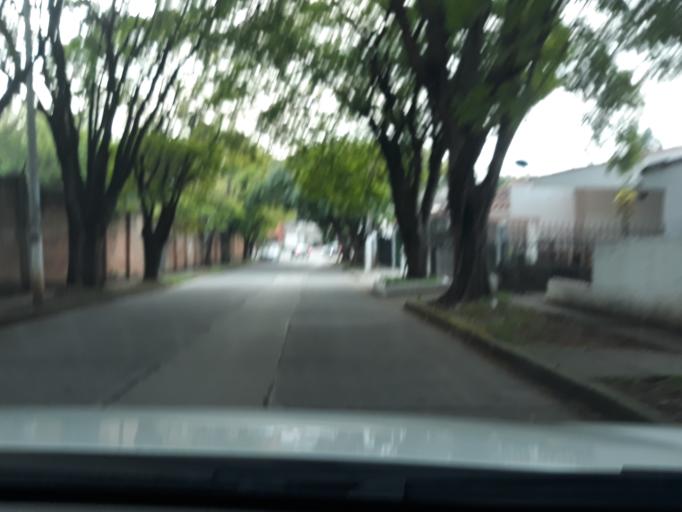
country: CO
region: Valle del Cauca
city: Cali
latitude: 3.4290
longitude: -76.5481
